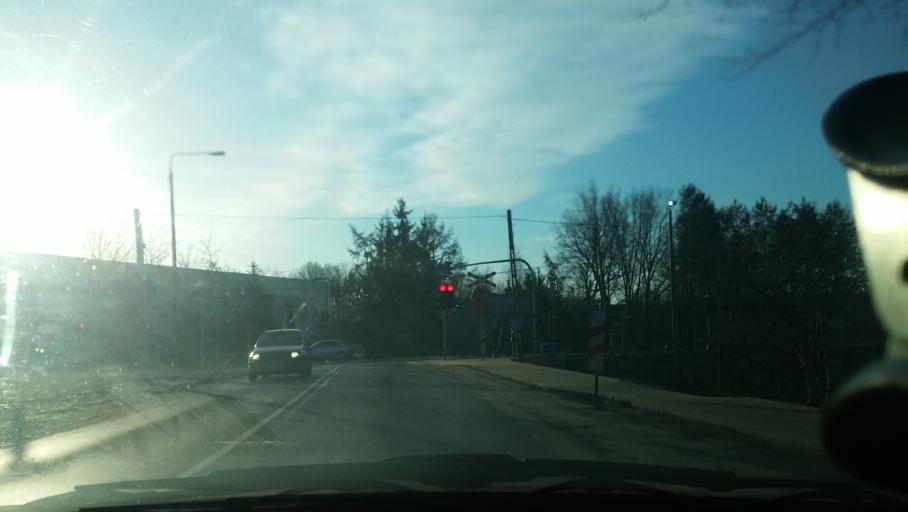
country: PL
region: Masovian Voivodeship
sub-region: Powiat piaseczynski
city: Piaseczno
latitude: 52.0659
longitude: 21.0191
